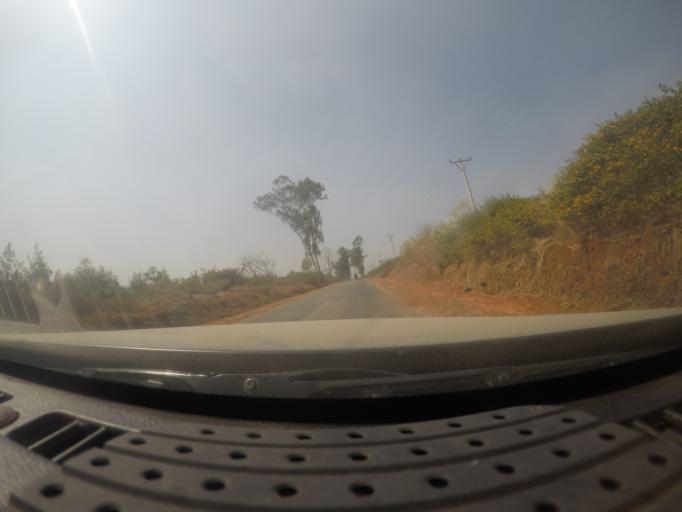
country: MM
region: Mandalay
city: Kyaukse
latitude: 21.1119
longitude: 96.4736
